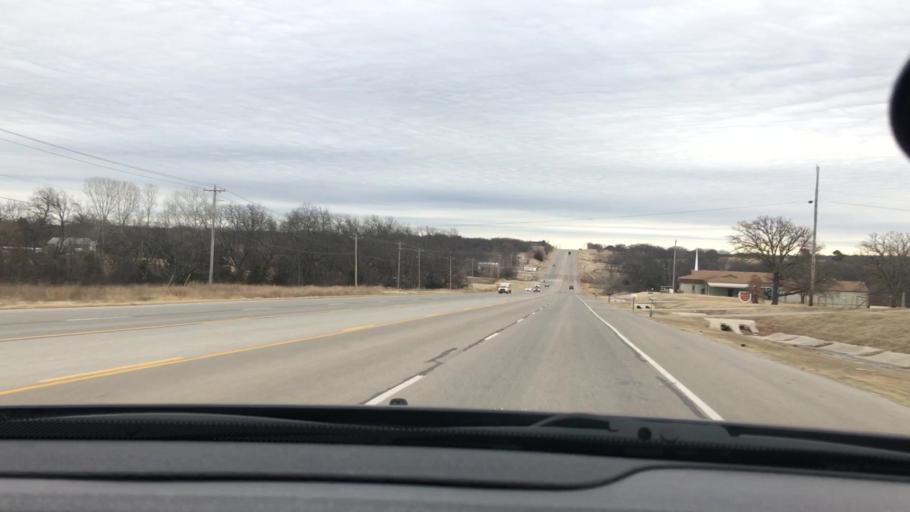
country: US
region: Oklahoma
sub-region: Carter County
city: Dickson
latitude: 34.1871
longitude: -97.0368
